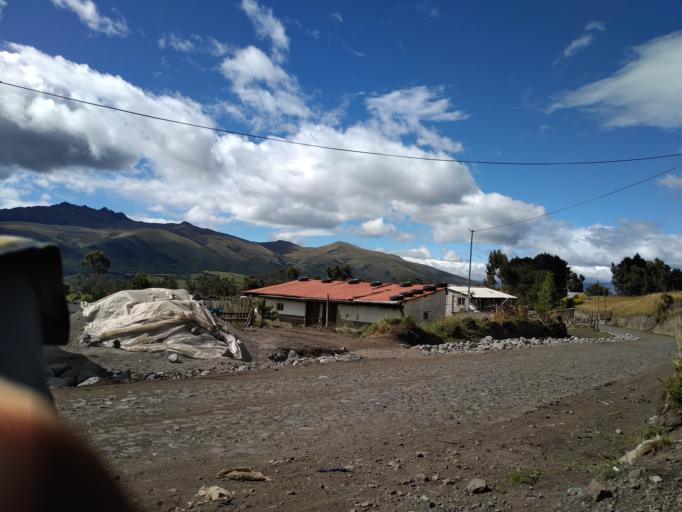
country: EC
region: Pichincha
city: Machachi
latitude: -0.5344
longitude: -78.4851
